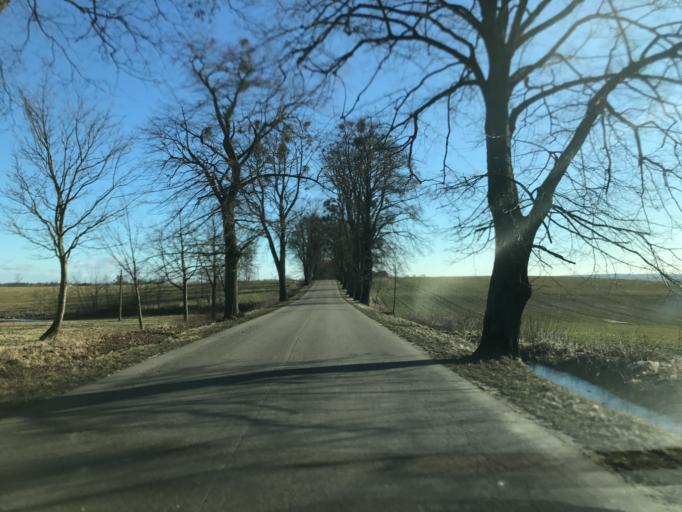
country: PL
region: Warmian-Masurian Voivodeship
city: Dobre Miasto
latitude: 53.9604
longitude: 20.3390
